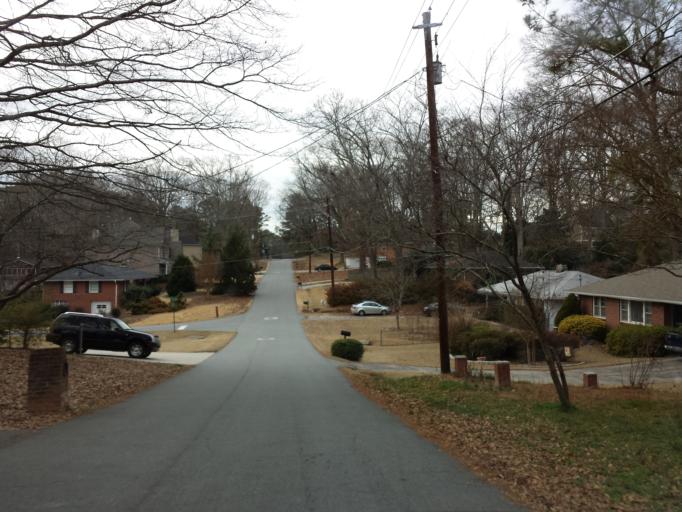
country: US
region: Georgia
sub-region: Cobb County
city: Smyrna
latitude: 33.9415
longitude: -84.4849
